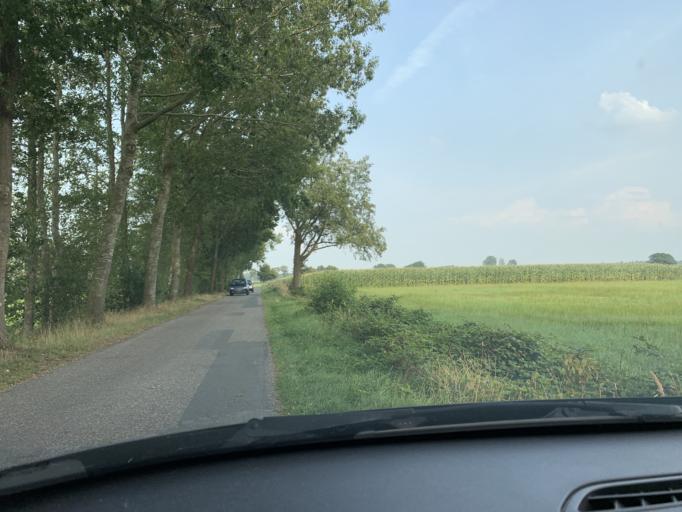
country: DE
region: Lower Saxony
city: Apen
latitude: 53.2365
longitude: 7.8172
